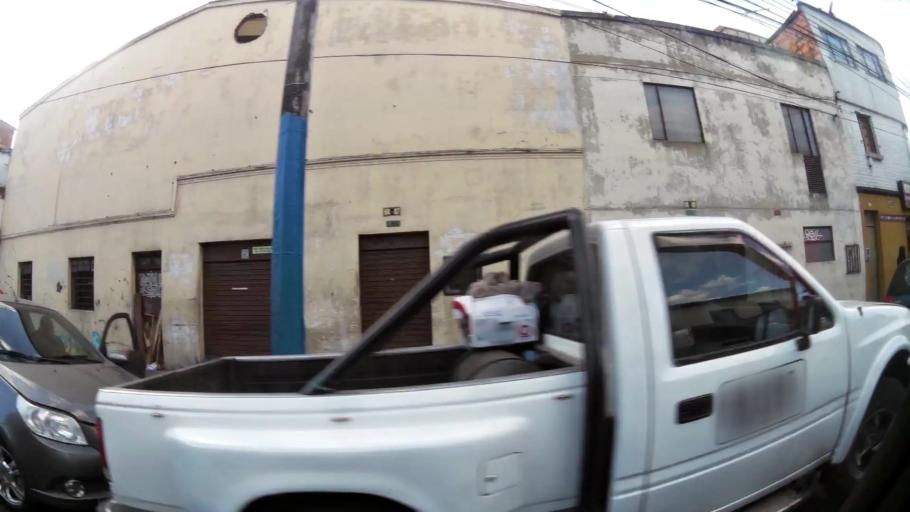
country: CO
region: Bogota D.C.
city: Bogota
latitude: 4.6587
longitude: -74.0748
